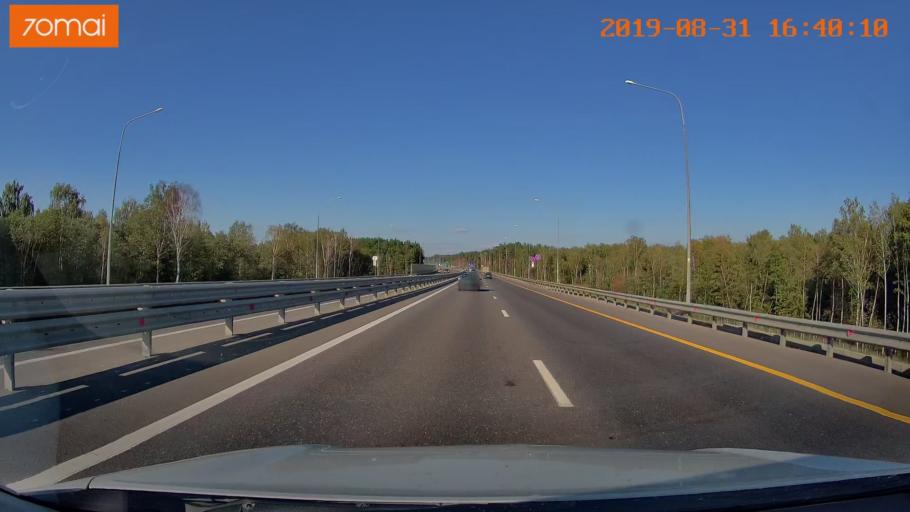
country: RU
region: Kaluga
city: Kurovskoye
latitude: 54.5617
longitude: 36.0432
